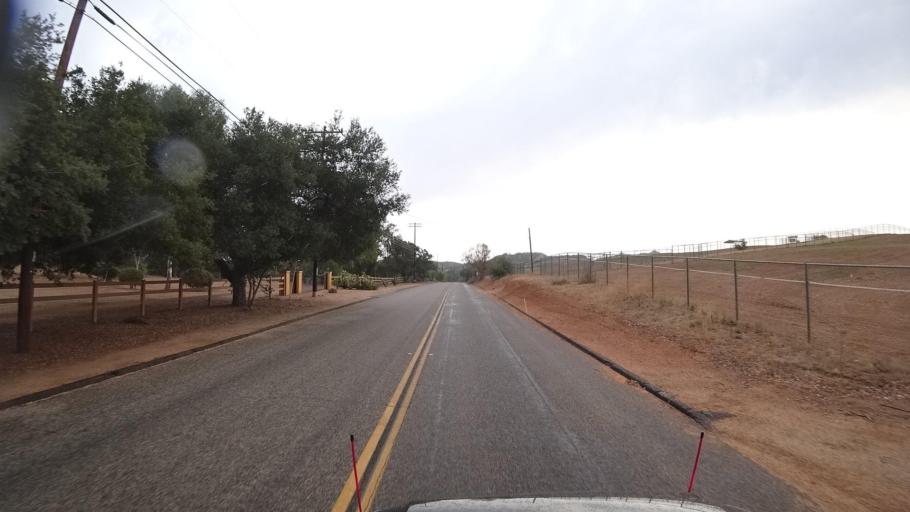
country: US
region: California
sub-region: San Diego County
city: Ramona
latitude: 32.9997
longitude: -116.9343
